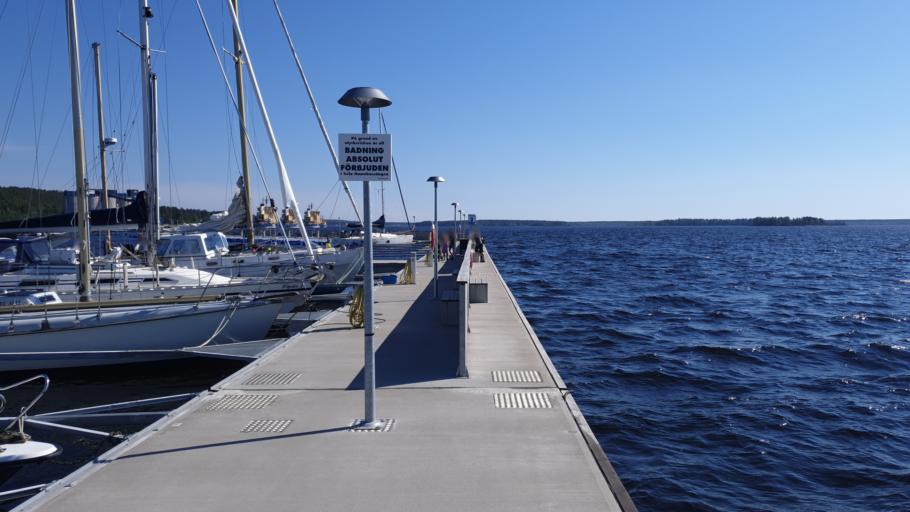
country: SE
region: Norrbotten
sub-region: Lulea Kommun
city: Lulea
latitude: 65.5795
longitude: 22.1604
